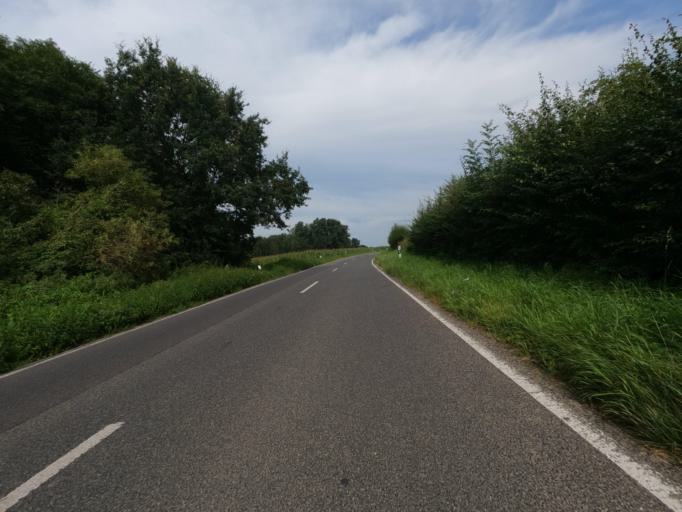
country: DE
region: North Rhine-Westphalia
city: Geilenkirchen
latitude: 50.9822
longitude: 6.1602
